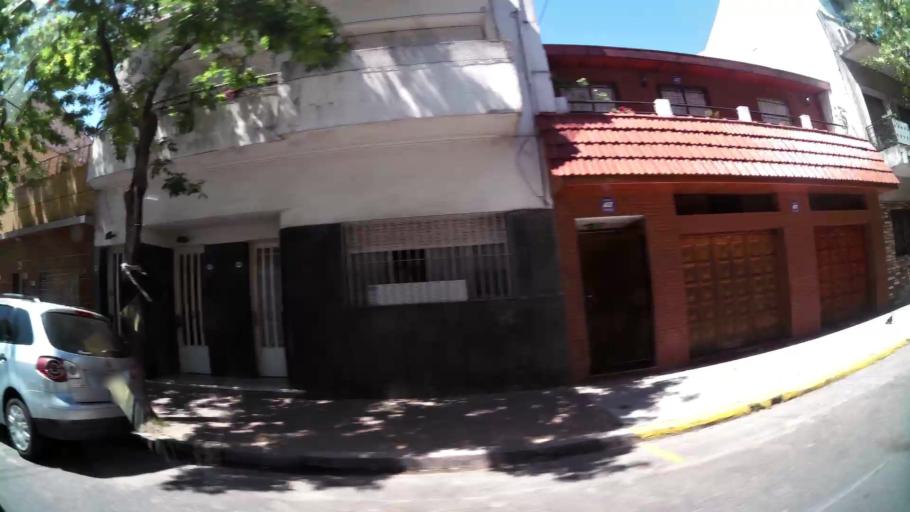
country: AR
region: Buenos Aires F.D.
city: Buenos Aires
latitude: -34.6283
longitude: -58.4076
